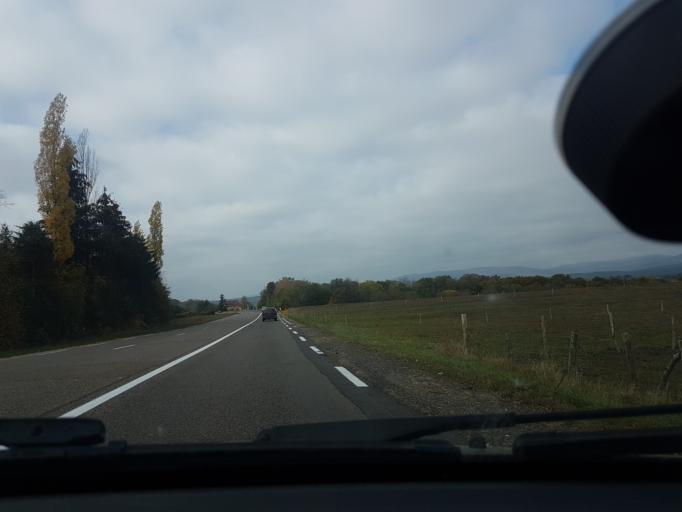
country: FR
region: Franche-Comte
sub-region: Departement de la Haute-Saone
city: Chalonvillars
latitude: 47.6480
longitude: 6.7706
